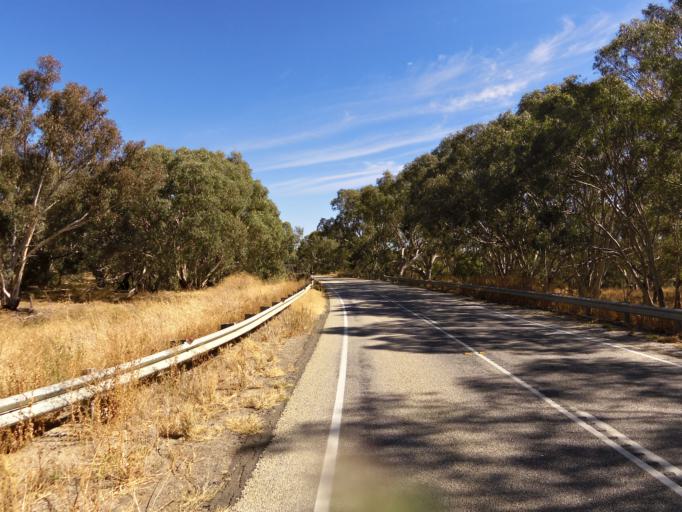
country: AU
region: Victoria
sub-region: Greater Bendigo
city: Long Gully
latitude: -36.1161
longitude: 143.8420
